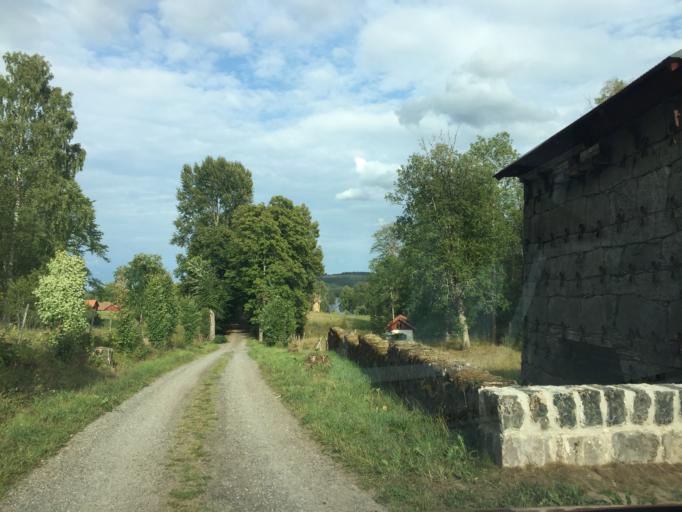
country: SE
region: Vaermland
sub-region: Filipstads Kommun
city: Lesjofors
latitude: 60.0252
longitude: 14.1051
